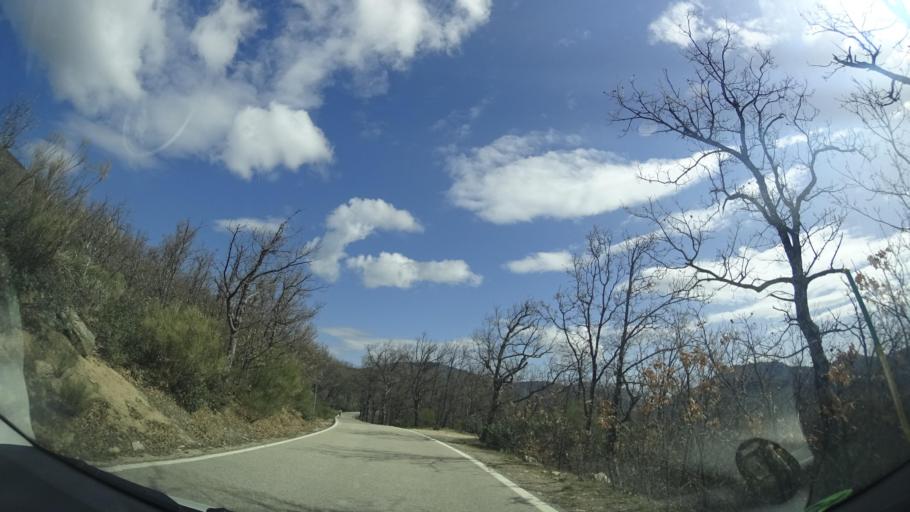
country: ES
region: Madrid
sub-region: Provincia de Madrid
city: Miraflores de la Sierra
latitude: 40.8371
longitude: -3.7688
